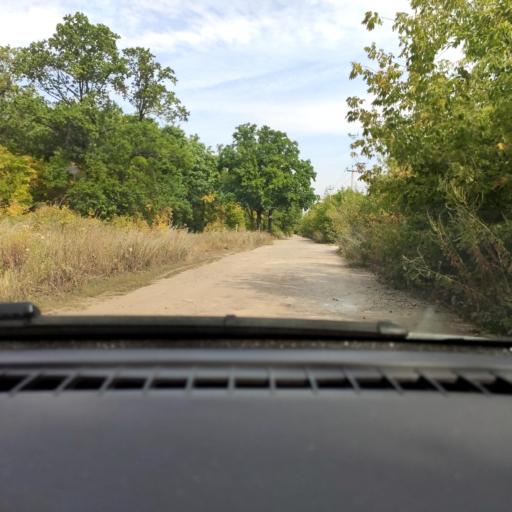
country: RU
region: Voronezj
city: Pridonskoy
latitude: 51.7507
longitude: 39.0765
